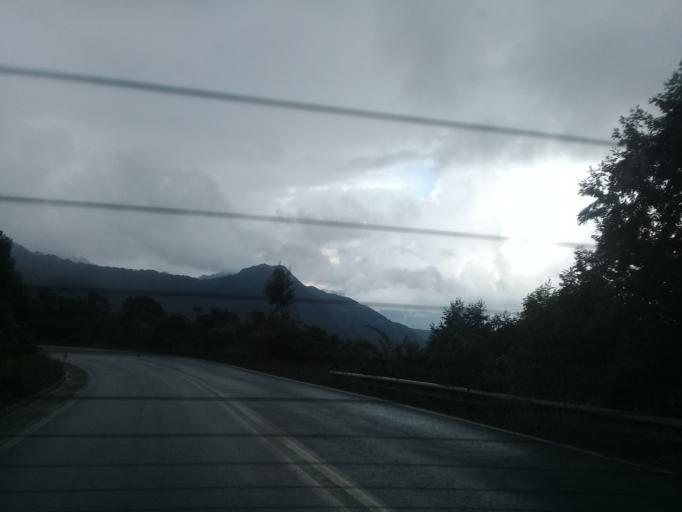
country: CO
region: Cundinamarca
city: Junin
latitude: 4.8543
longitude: -73.7534
